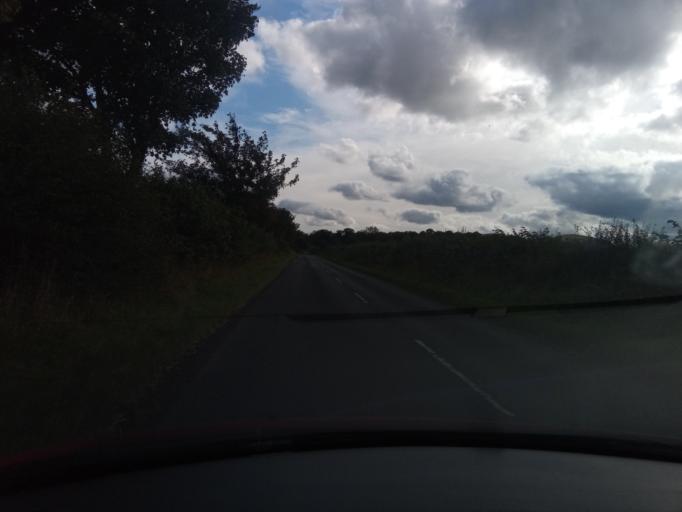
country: GB
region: Scotland
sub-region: The Scottish Borders
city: Kelso
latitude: 55.5258
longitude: -2.3578
